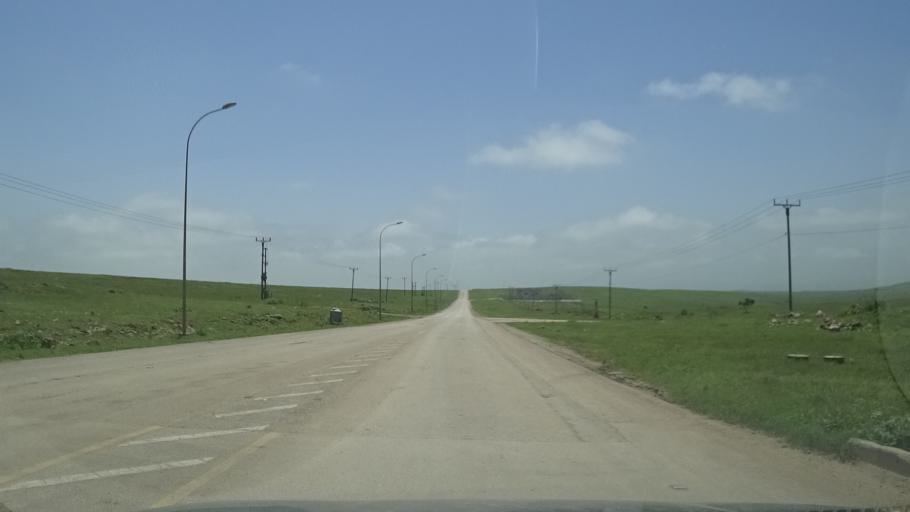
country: OM
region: Zufar
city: Salalah
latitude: 17.2386
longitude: 54.2855
